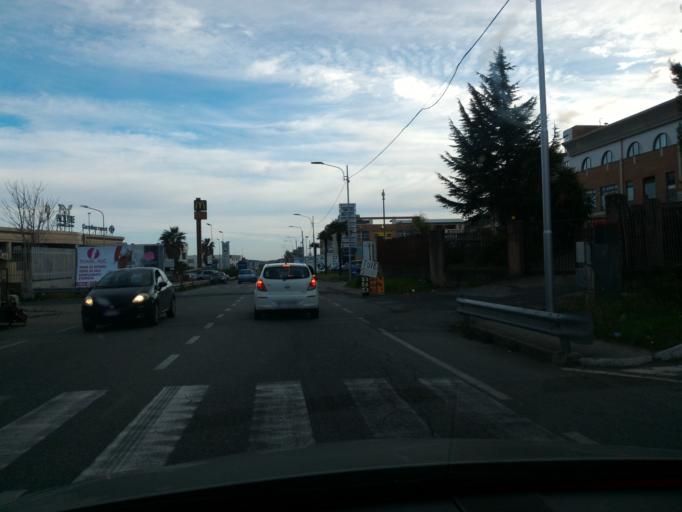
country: IT
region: Calabria
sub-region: Provincia di Catanzaro
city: Catanzaro
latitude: 38.8859
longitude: 16.5978
